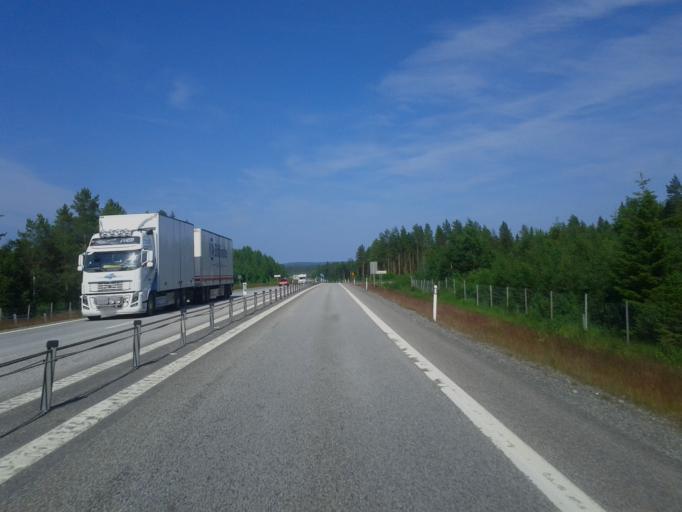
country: SE
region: Vaesterbotten
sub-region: Umea Kommun
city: Hoernefors
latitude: 63.6535
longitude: 19.9519
